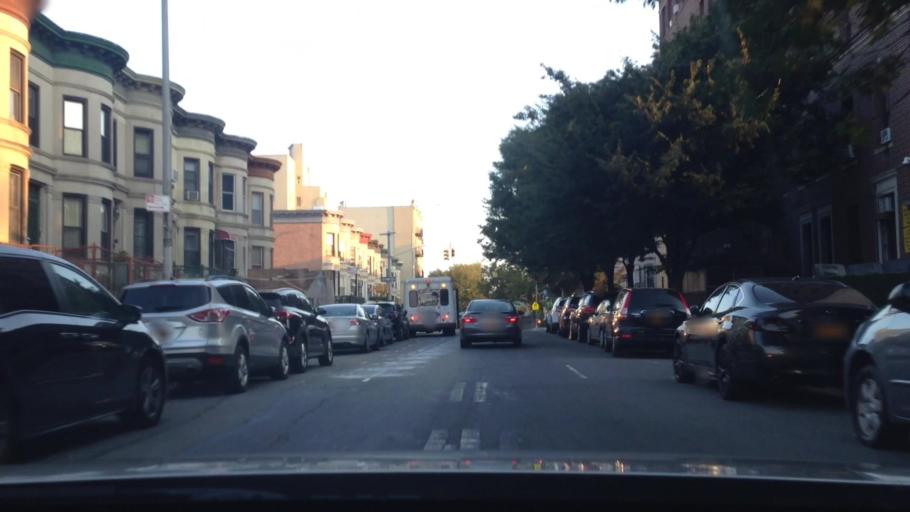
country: US
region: New York
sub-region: Kings County
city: Brooklyn
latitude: 40.6666
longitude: -73.9482
